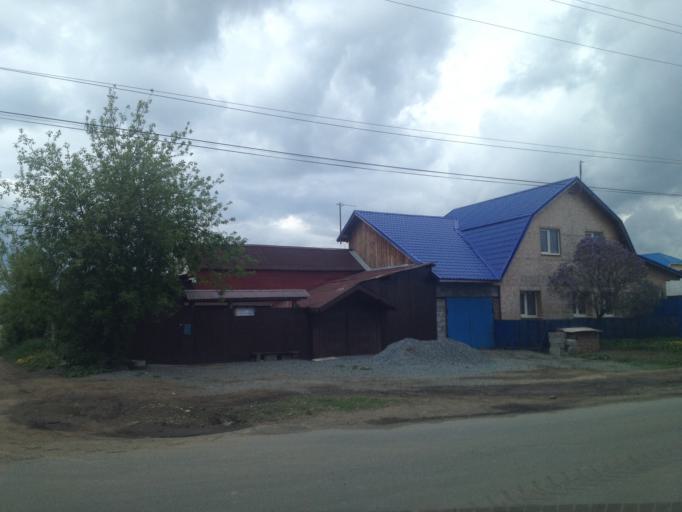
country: RU
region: Sverdlovsk
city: Aramil
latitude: 56.6859
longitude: 60.8544
